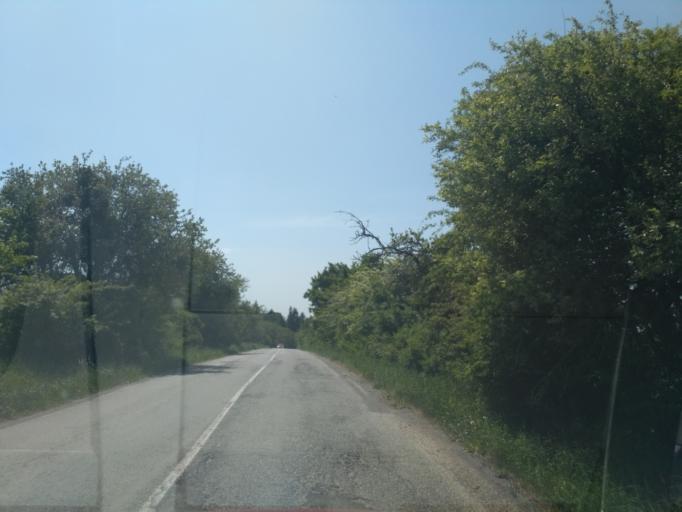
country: SK
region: Kosicky
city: Kosice
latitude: 48.8042
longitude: 21.3991
